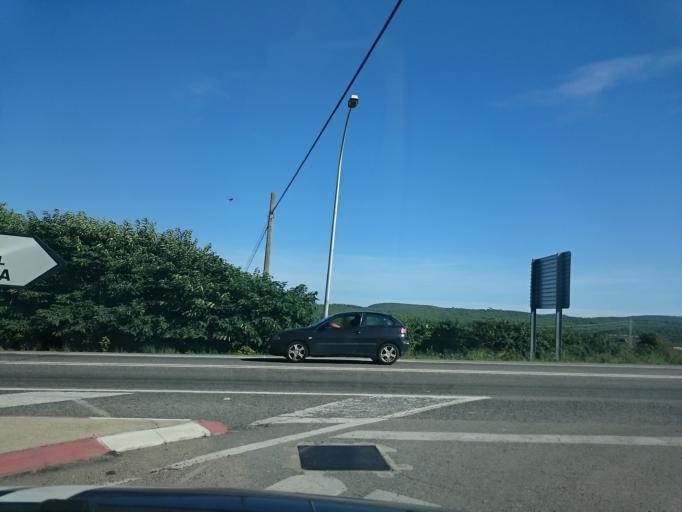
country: ES
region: Catalonia
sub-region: Provincia de Barcelona
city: Castellet
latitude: 41.2676
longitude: 1.6066
